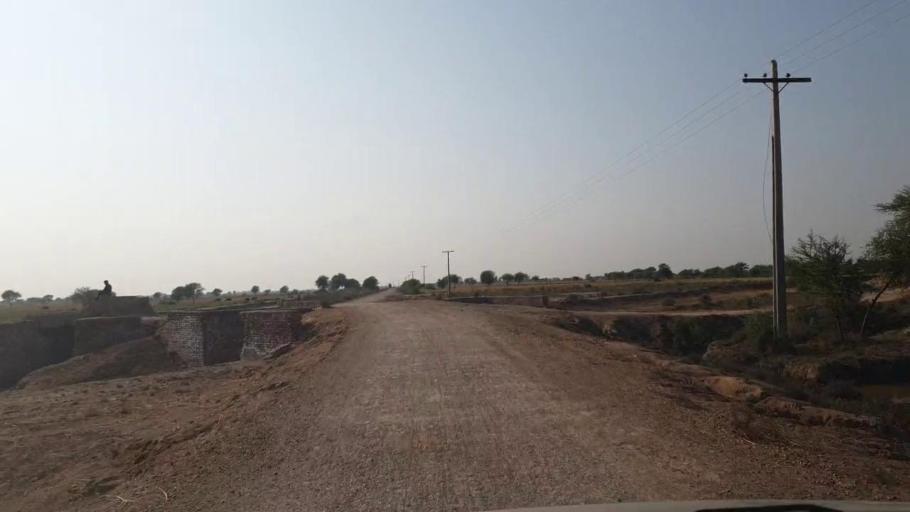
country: PK
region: Sindh
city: Kario
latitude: 24.8920
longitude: 68.6410
